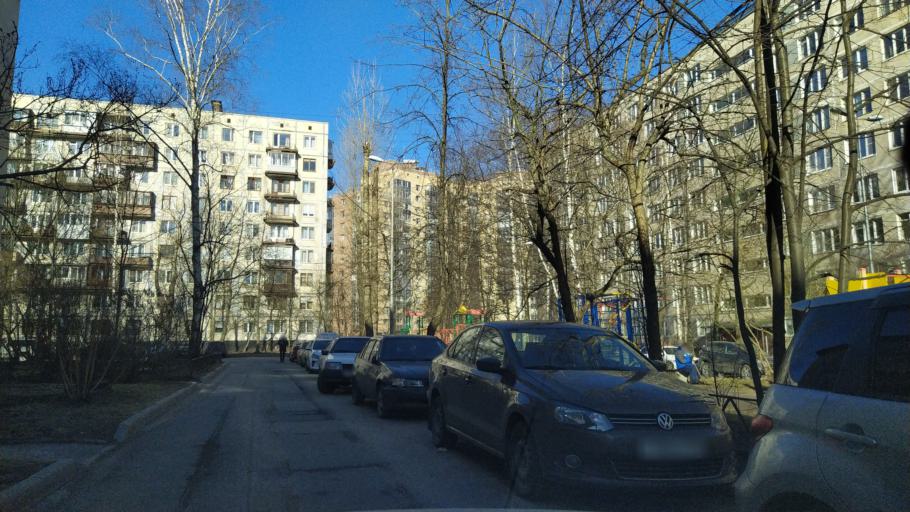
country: RU
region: Leningrad
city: Akademicheskoe
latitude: 60.0147
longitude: 30.4077
